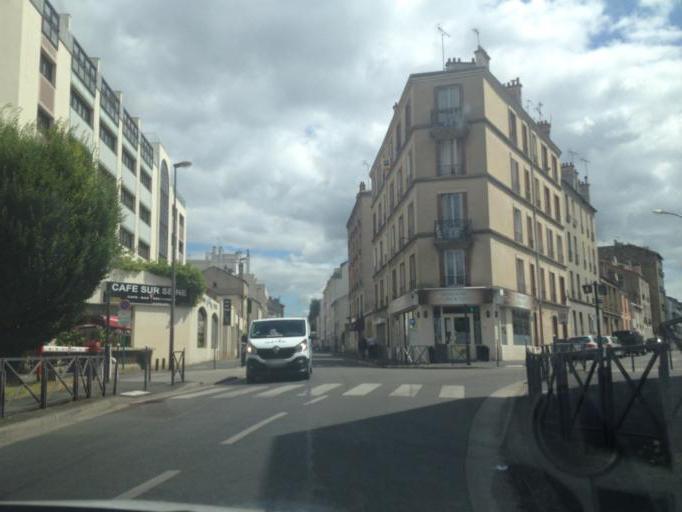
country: FR
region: Ile-de-France
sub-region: Departement du Val-de-Marne
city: Ivry-sur-Seine
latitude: 48.8130
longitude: 2.3934
